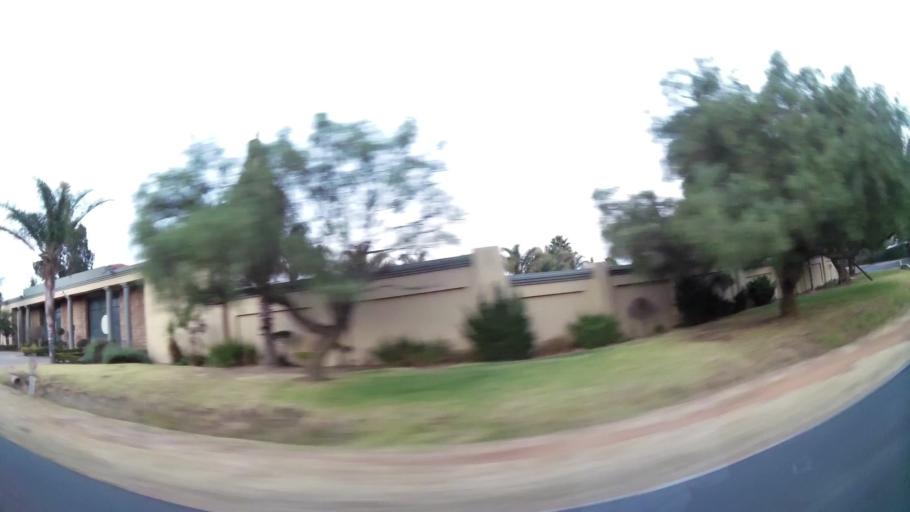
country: ZA
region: Gauteng
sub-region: City of Johannesburg Metropolitan Municipality
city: Diepsloot
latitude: -25.9701
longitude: 28.0648
